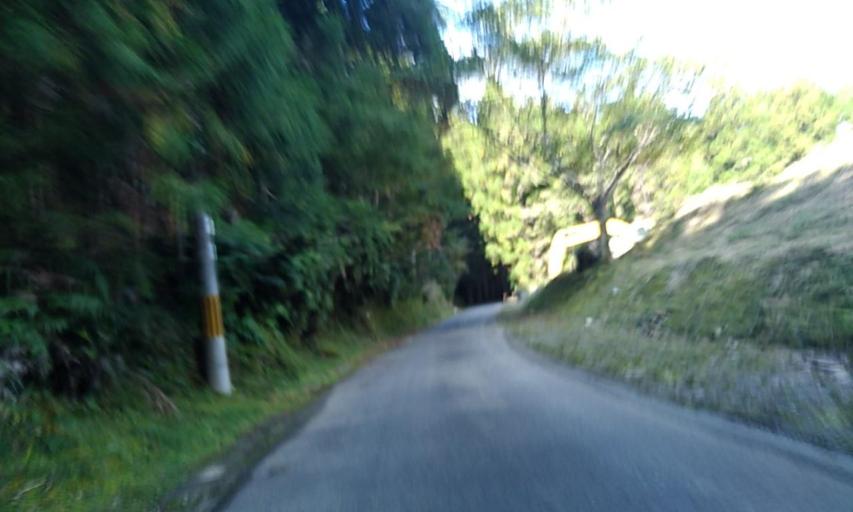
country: JP
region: Wakayama
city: Shingu
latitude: 33.9152
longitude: 135.9898
